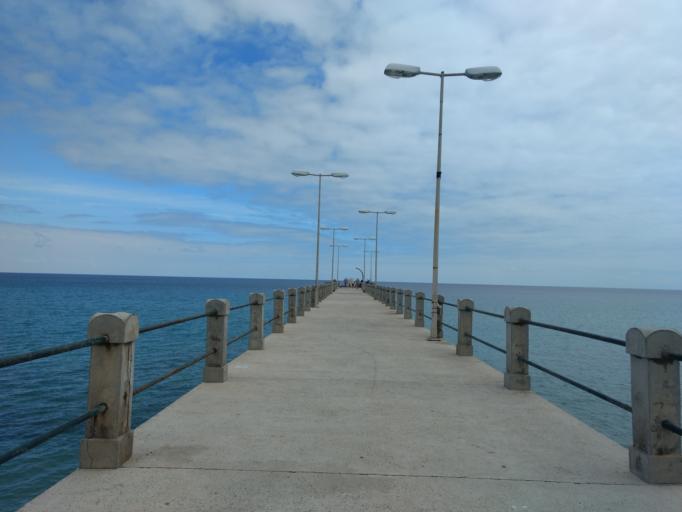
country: PT
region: Madeira
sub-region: Porto Santo
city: Vila de Porto Santo
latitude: 33.0572
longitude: -16.3344
